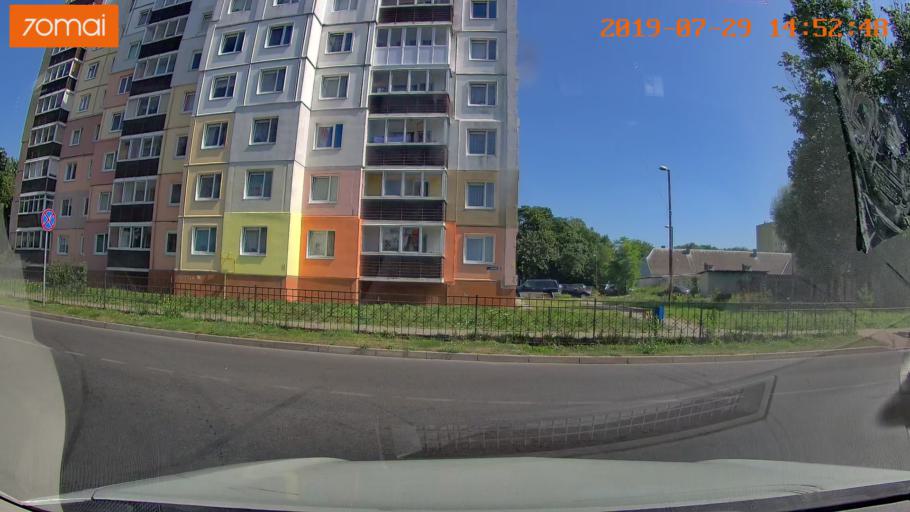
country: RU
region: Kaliningrad
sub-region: Gorod Kaliningrad
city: Baltiysk
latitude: 54.6614
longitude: 19.9151
